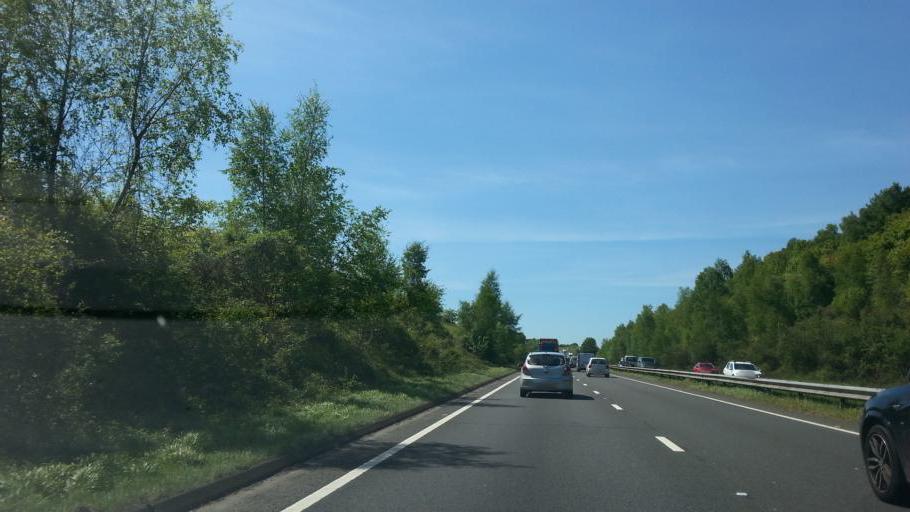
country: GB
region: England
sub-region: Hampshire
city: Andover
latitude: 51.1978
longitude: -1.4323
